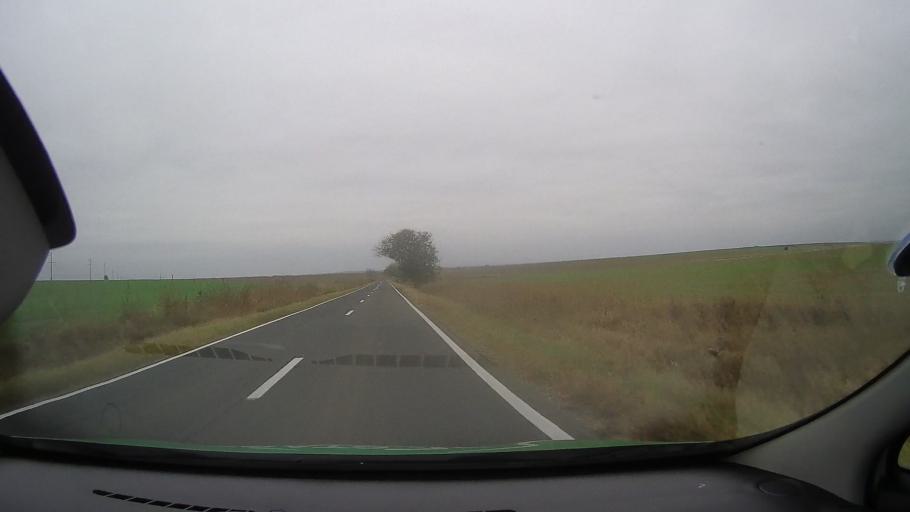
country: RO
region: Constanta
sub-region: Comuna Saraiu
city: Saraiu
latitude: 44.7109
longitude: 28.1137
